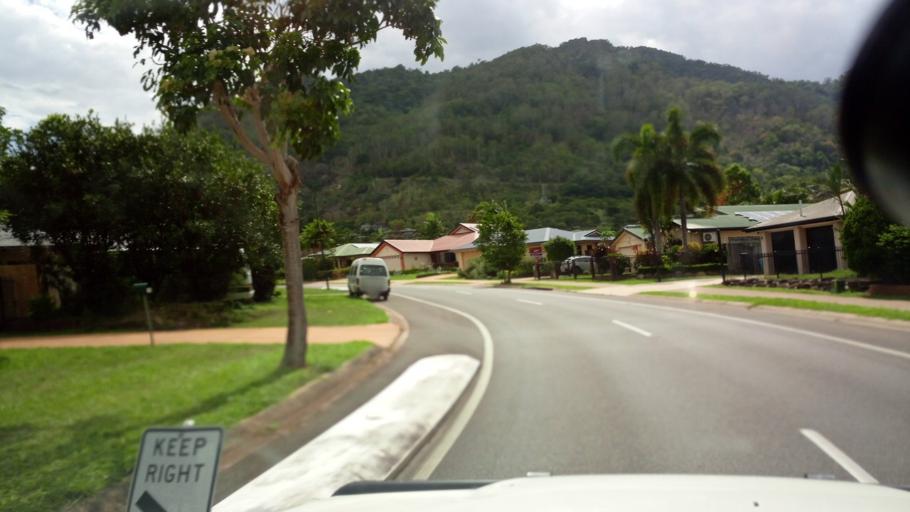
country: AU
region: Queensland
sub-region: Cairns
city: Woree
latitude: -16.9244
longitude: 145.7279
